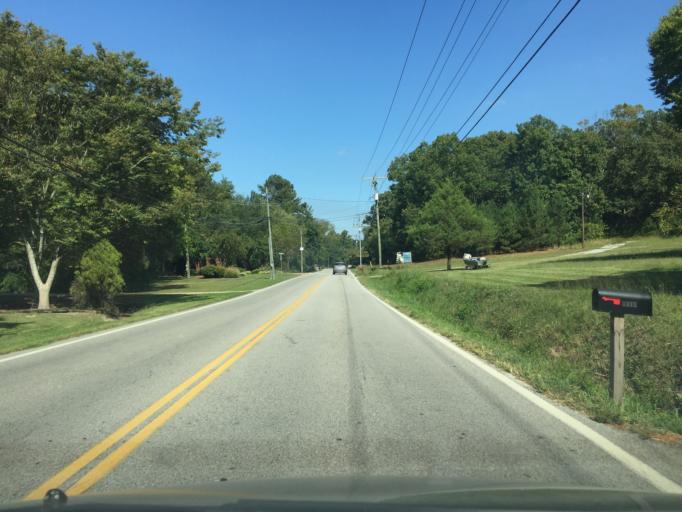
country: US
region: Tennessee
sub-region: Hamilton County
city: Collegedale
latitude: 35.0915
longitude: -85.0787
